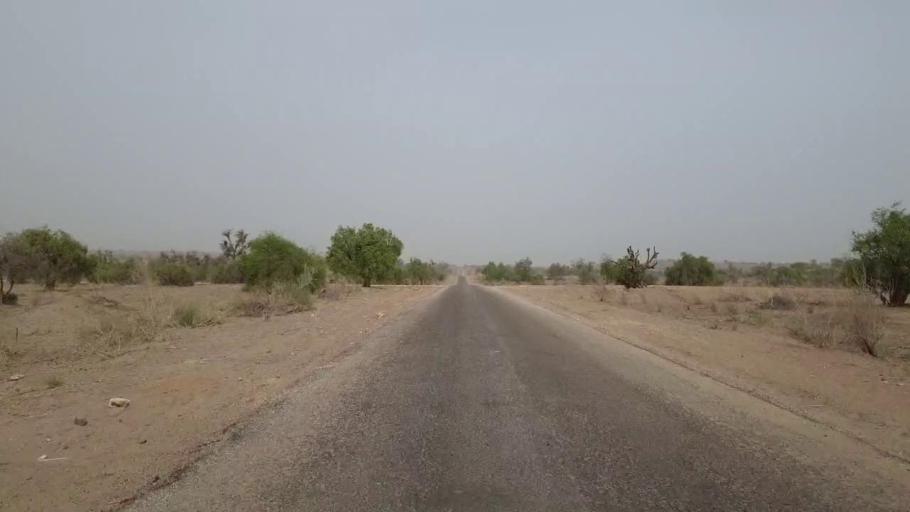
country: PK
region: Sindh
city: Islamkot
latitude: 24.5665
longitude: 70.3297
